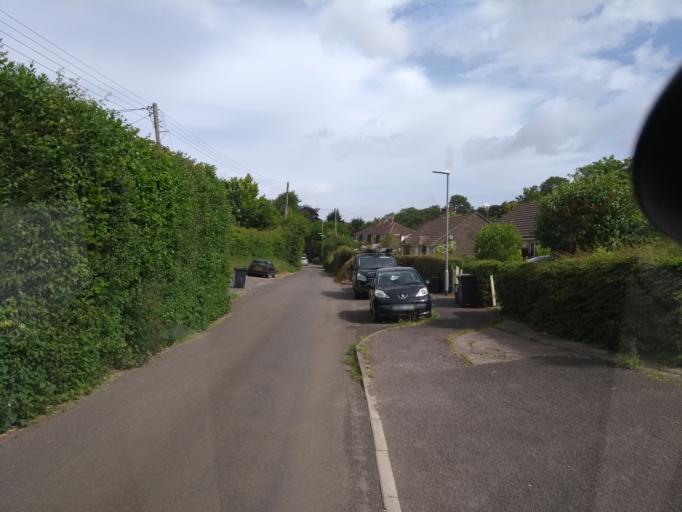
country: GB
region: England
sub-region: Somerset
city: Williton
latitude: 51.1810
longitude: -3.2179
